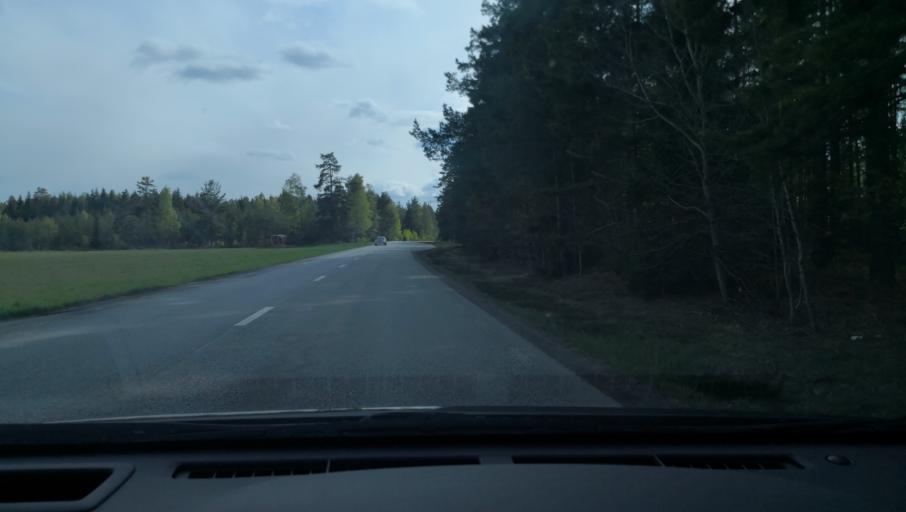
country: SE
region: OErebro
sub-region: Askersunds Kommun
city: Asbro
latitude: 59.0495
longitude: 15.0457
